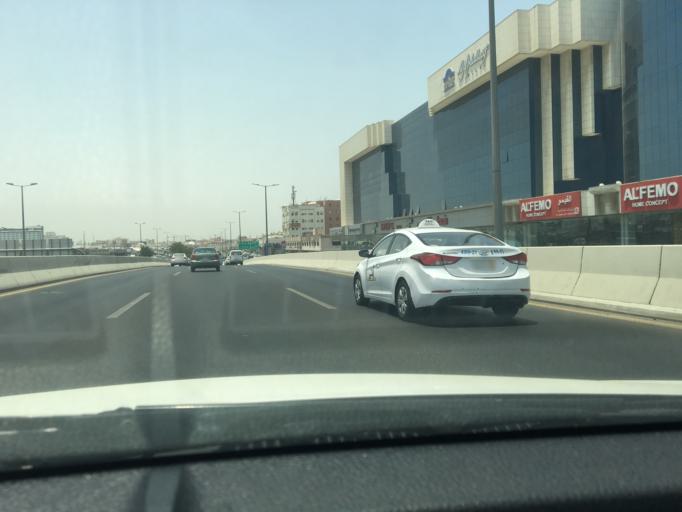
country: SA
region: Makkah
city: Jeddah
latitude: 21.5753
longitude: 39.1799
